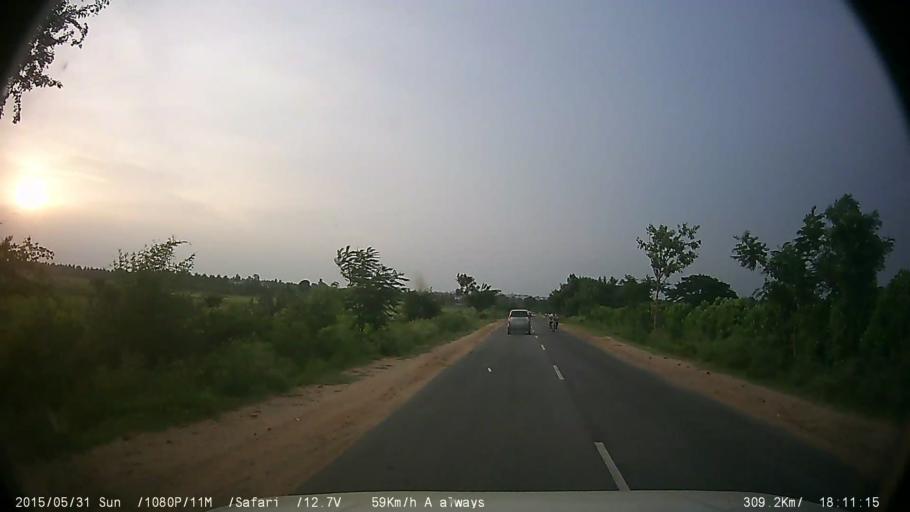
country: IN
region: Karnataka
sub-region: Mysore
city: Nanjangud
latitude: 12.0859
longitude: 76.6747
